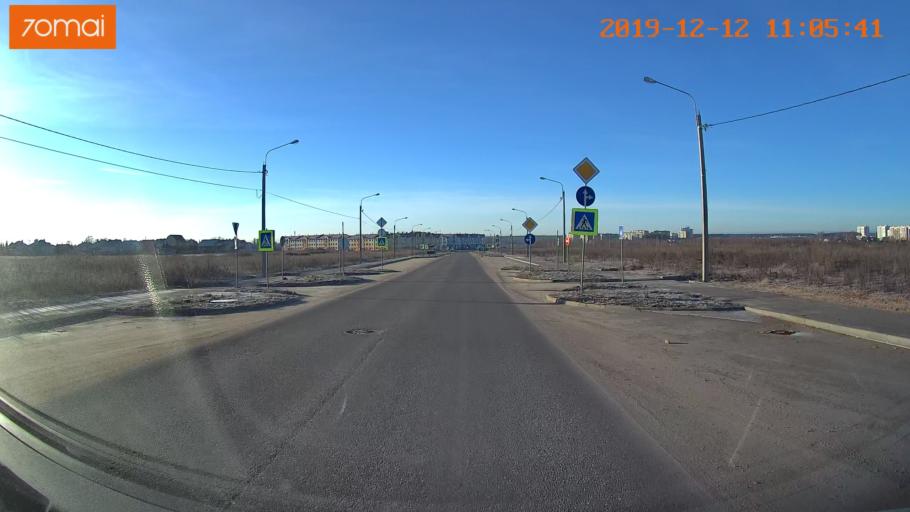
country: RU
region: Ivanovo
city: Kokhma
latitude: 56.9476
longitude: 41.0949
